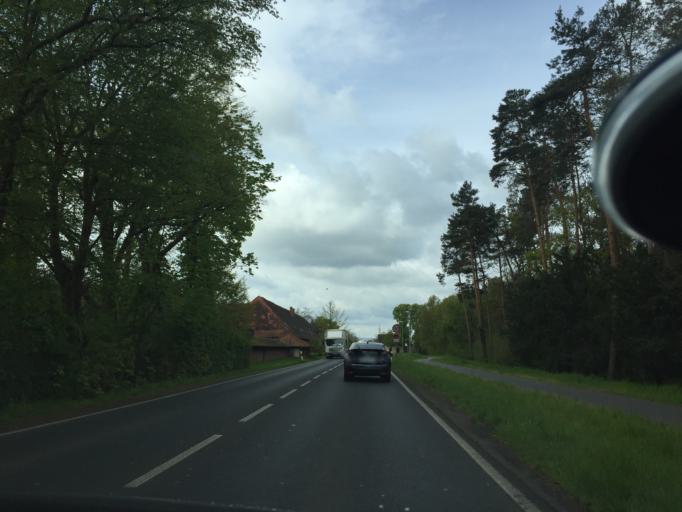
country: DE
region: Bavaria
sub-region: Regierungsbezirk Unterfranken
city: Mainaschaff
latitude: 49.9519
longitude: 9.1120
